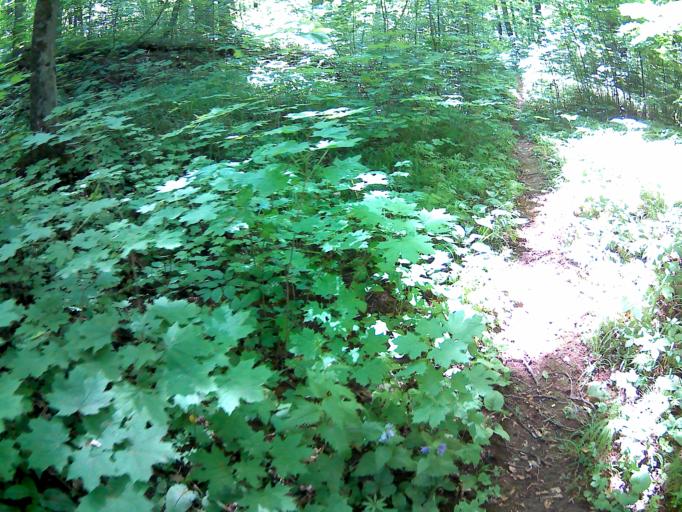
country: RU
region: Nizjnij Novgorod
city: Nizhniy Novgorod
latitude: 56.2295
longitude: 43.9248
